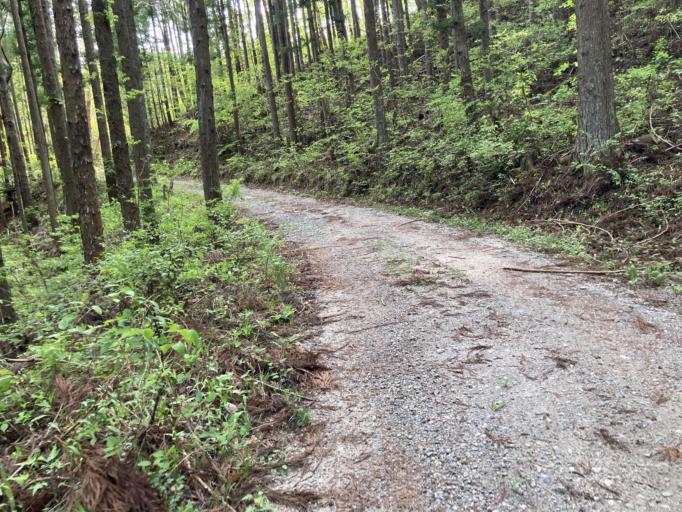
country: JP
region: Fukushima
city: Iwaki
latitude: 37.1657
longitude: 140.7992
